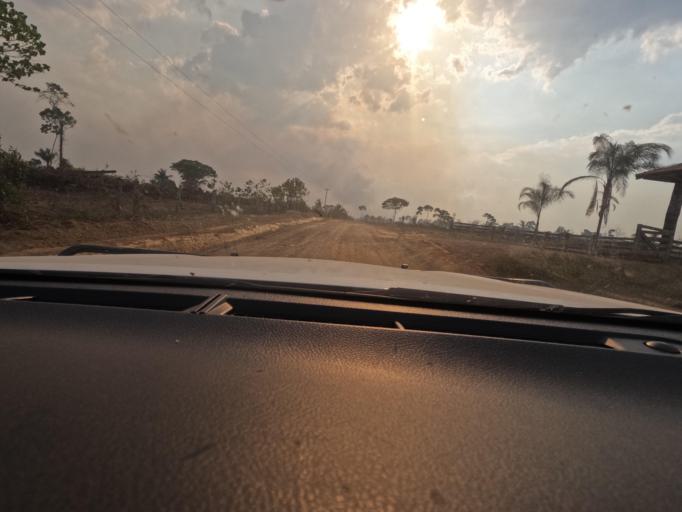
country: BR
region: Rondonia
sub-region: Porto Velho
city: Porto Velho
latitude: -8.6383
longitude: -63.1725
